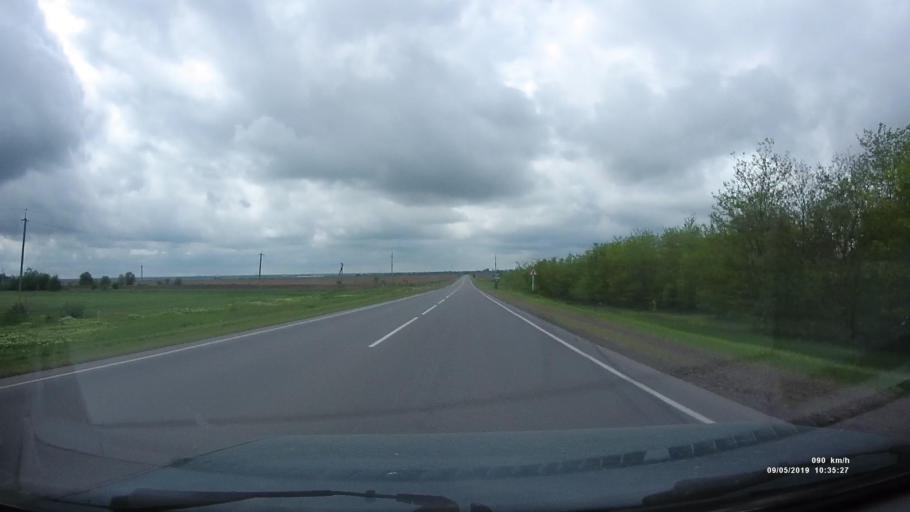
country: RU
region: Rostov
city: Peshkovo
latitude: 47.0430
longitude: 39.4138
